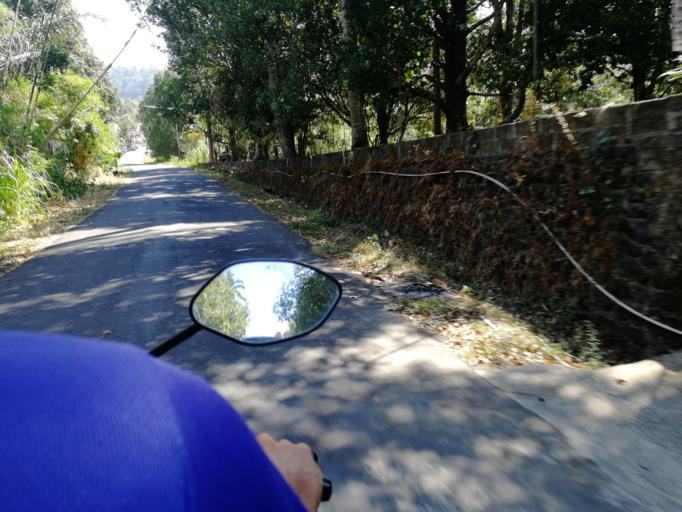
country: ID
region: Bali
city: Banjar Kedisan
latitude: -8.1639
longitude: 115.3042
